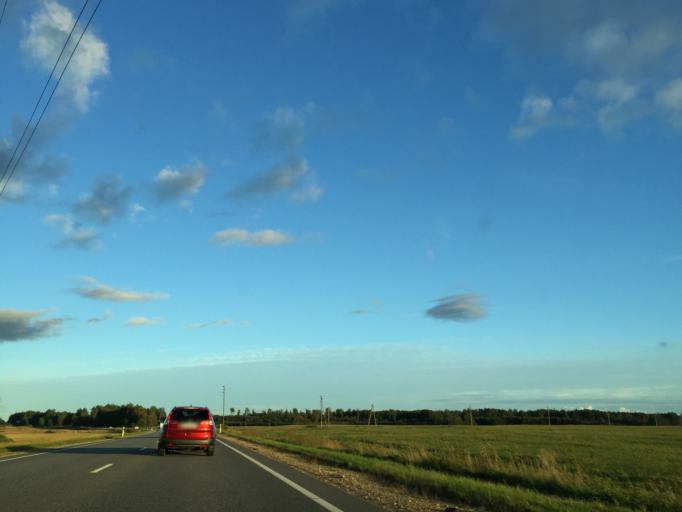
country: LV
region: Broceni
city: Broceni
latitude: 56.6639
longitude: 22.6000
